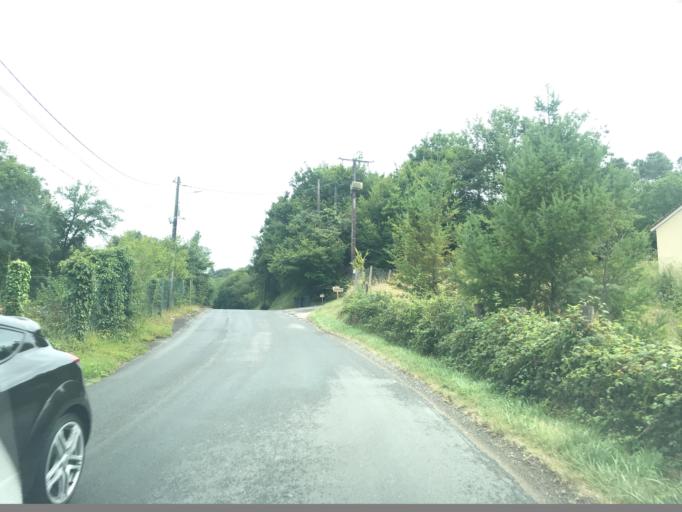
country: FR
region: Aquitaine
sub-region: Departement de la Dordogne
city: Chancelade
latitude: 45.1794
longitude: 0.6702
